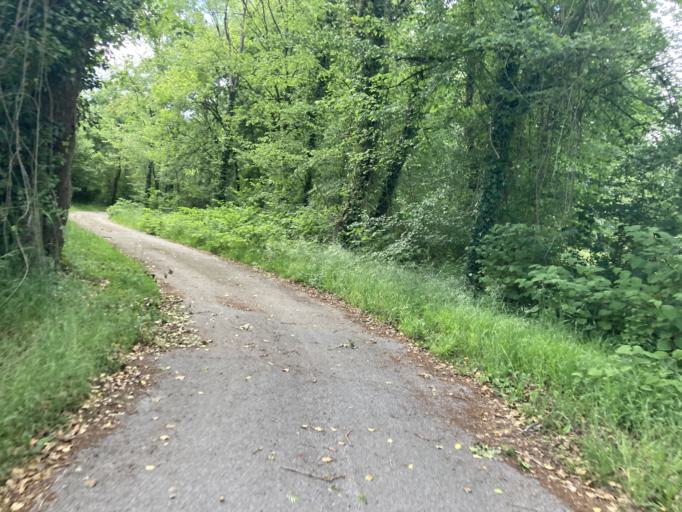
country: FR
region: Aquitaine
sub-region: Departement des Pyrenees-Atlantiques
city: Denguin
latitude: 43.3506
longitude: -0.5140
